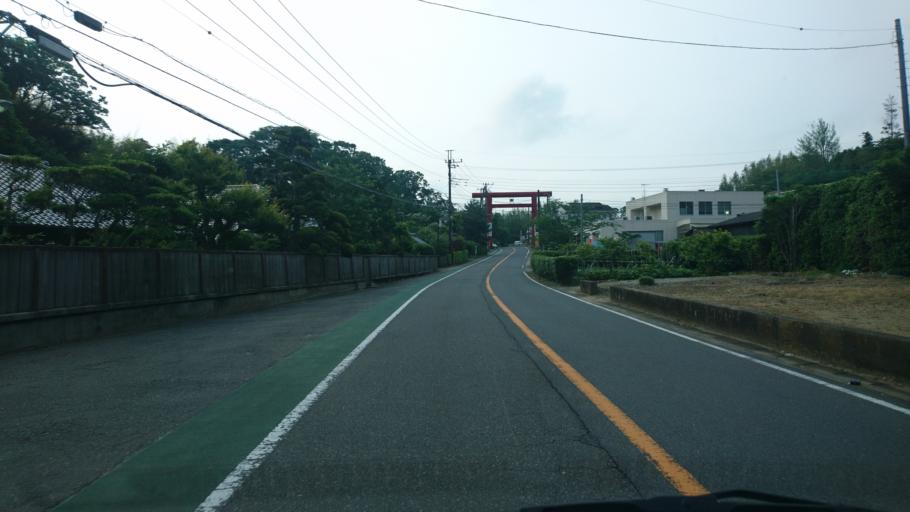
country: JP
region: Ibaraki
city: Edosaki
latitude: 35.8758
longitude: 140.3504
